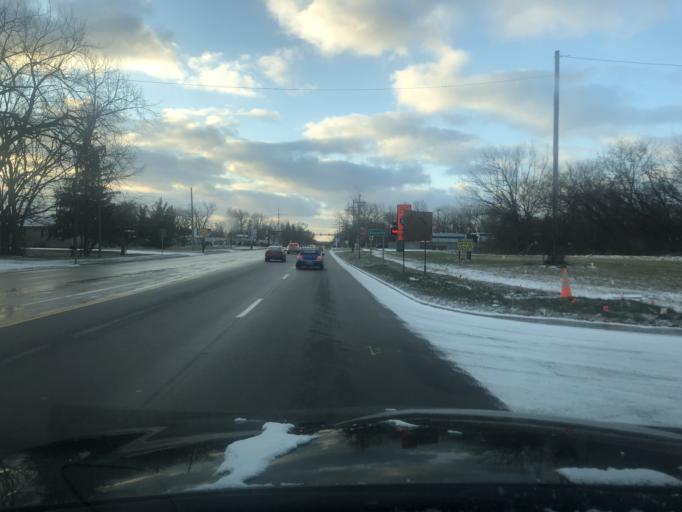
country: US
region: Michigan
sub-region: Wayne County
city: Wayne
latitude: 42.2551
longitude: -83.3479
